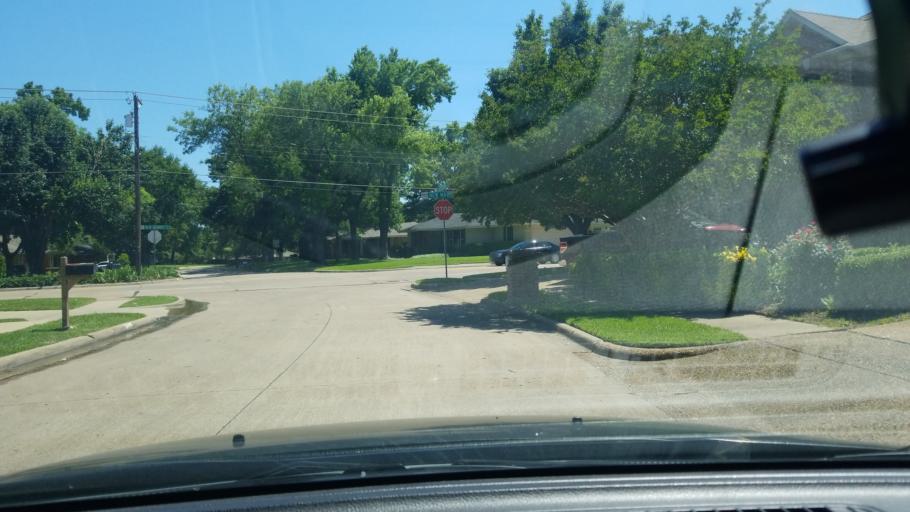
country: US
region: Texas
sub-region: Dallas County
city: Mesquite
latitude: 32.7562
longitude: -96.6021
